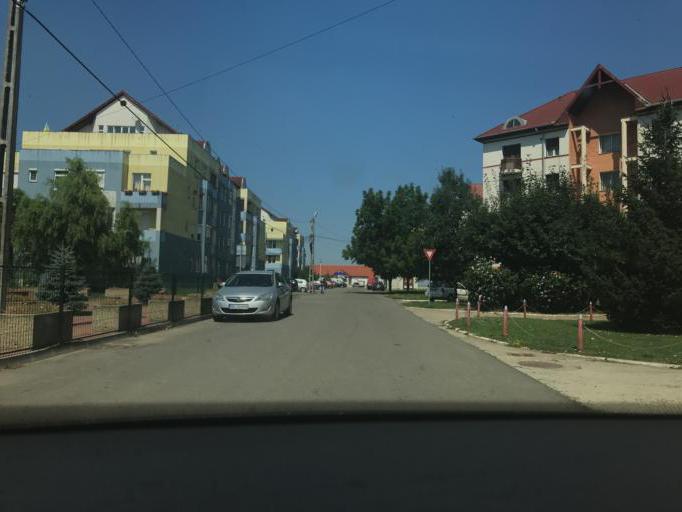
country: RO
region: Bihor
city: Margita
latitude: 47.3546
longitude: 22.3487
